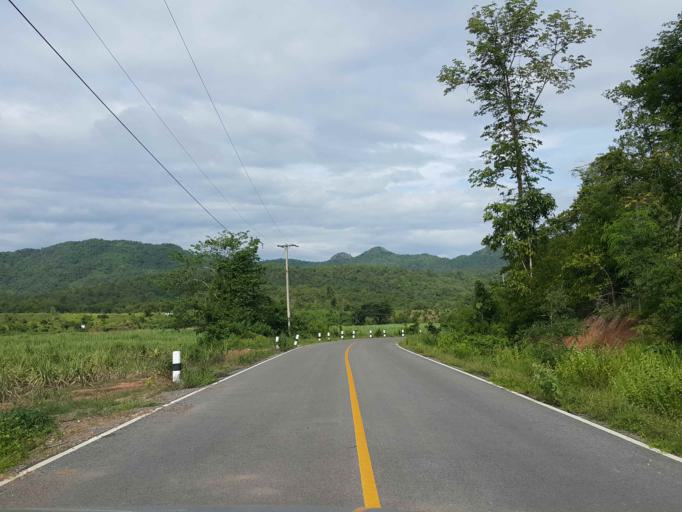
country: TH
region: Sukhothai
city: Thung Saliam
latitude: 17.2383
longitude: 99.5015
